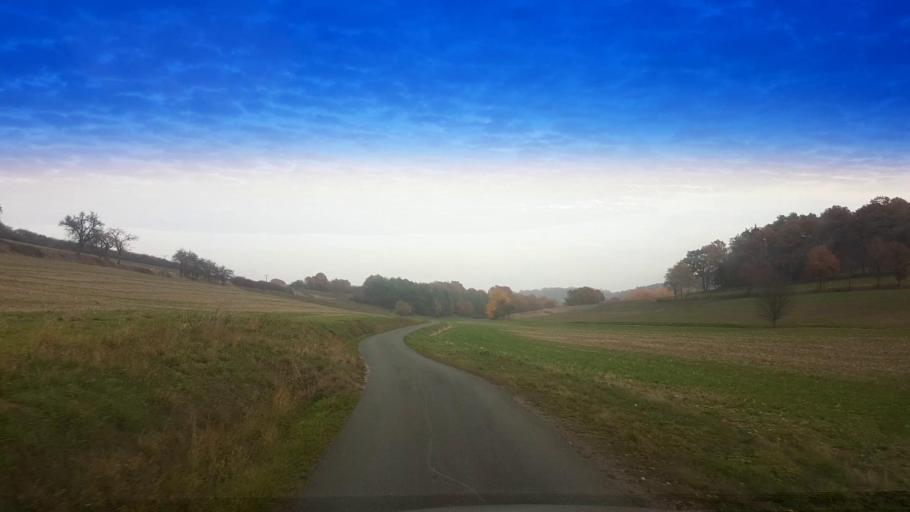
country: DE
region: Bavaria
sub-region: Upper Franconia
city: Viereth-Trunstadt
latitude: 49.9217
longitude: 10.7507
